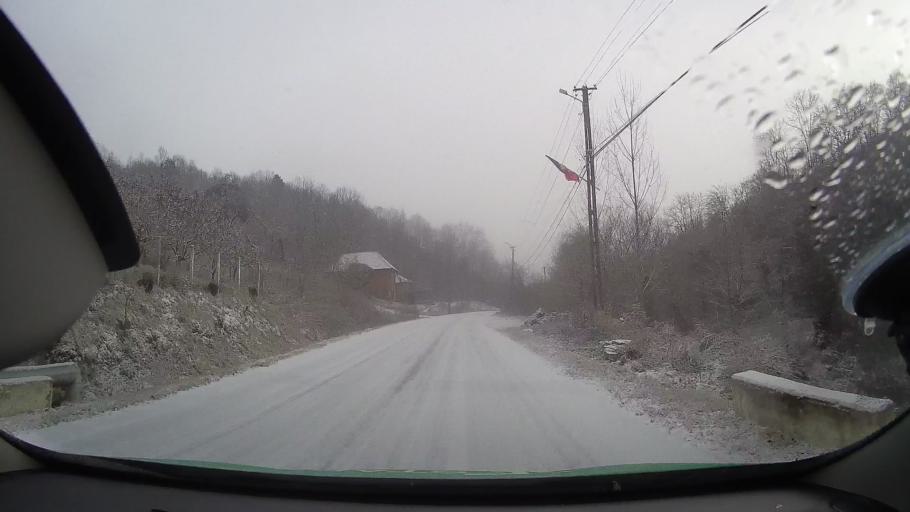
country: RO
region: Alba
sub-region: Comuna Livezile
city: Livezile
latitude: 46.3662
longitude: 23.5959
